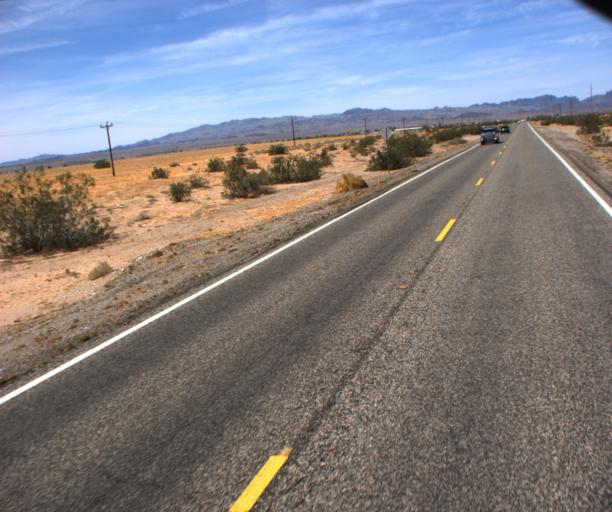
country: US
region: Arizona
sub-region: La Paz County
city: Parker
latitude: 34.1102
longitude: -114.2781
